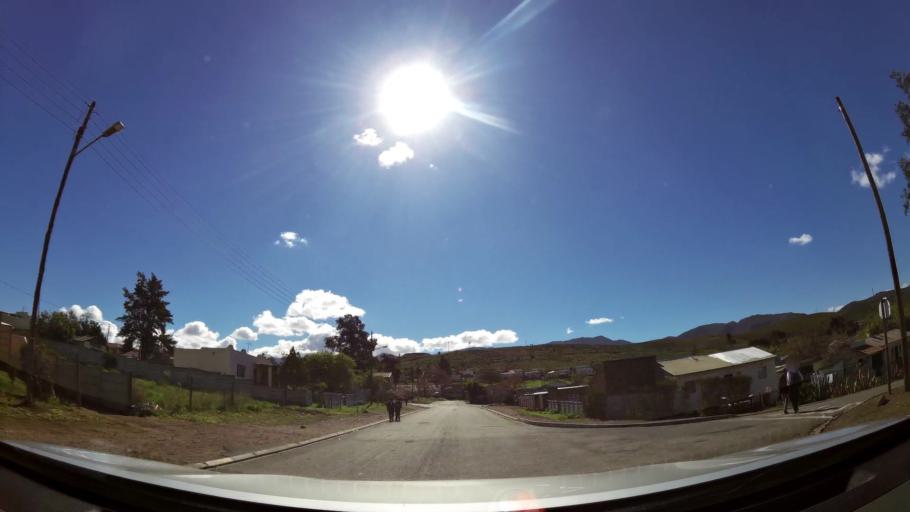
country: ZA
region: Western Cape
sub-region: Cape Winelands District Municipality
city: Ashton
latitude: -33.8322
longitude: 20.0462
